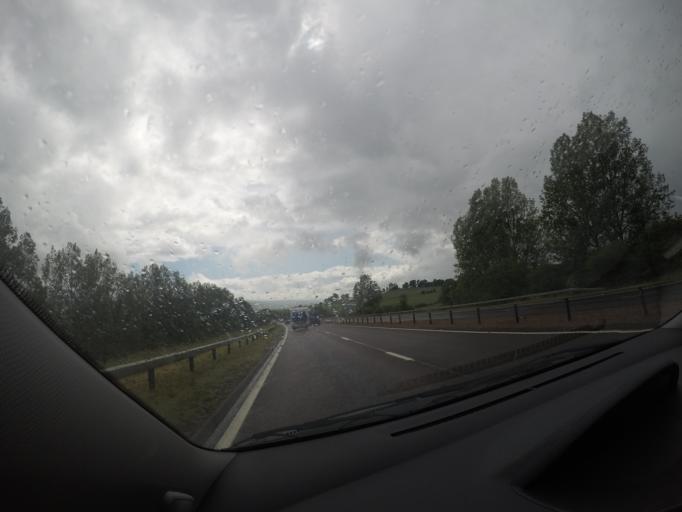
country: GB
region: Scotland
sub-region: Perth and Kinross
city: Methven
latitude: 56.3509
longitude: -3.5750
